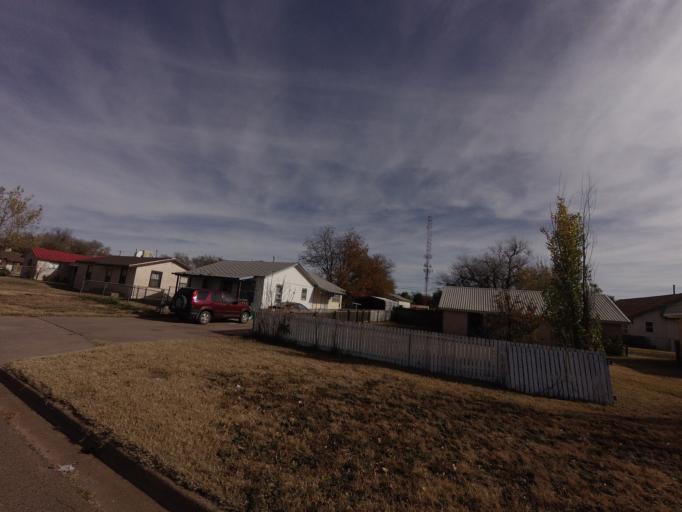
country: US
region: New Mexico
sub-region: Curry County
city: Clovis
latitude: 34.4083
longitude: -103.1902
